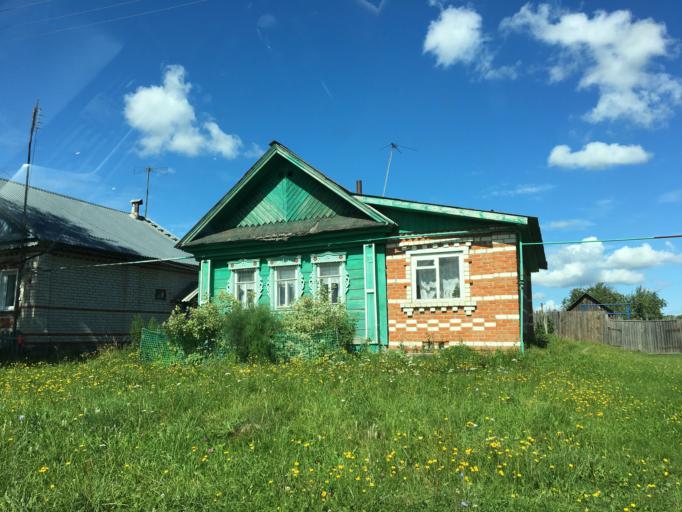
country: RU
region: Nizjnij Novgorod
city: Lyskovo
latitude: 55.9831
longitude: 45.0328
